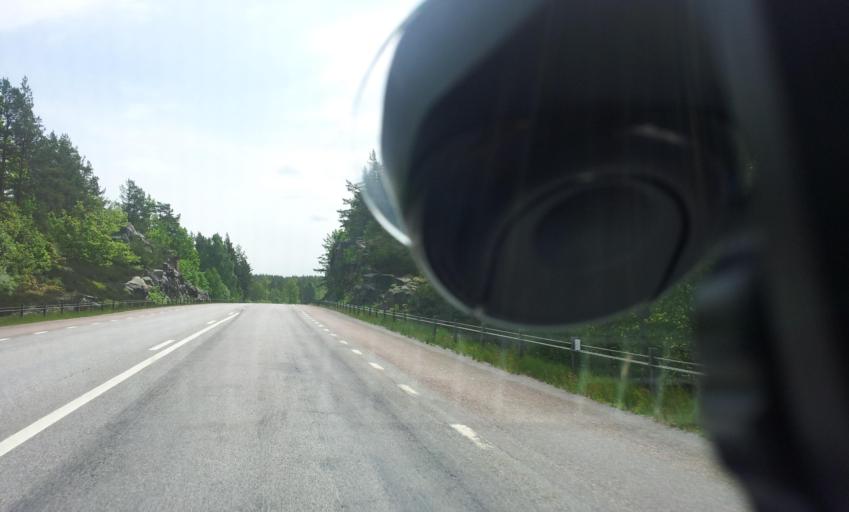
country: SE
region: Kalmar
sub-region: Vasterviks Kommun
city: Ankarsrum
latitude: 57.6359
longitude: 16.4520
